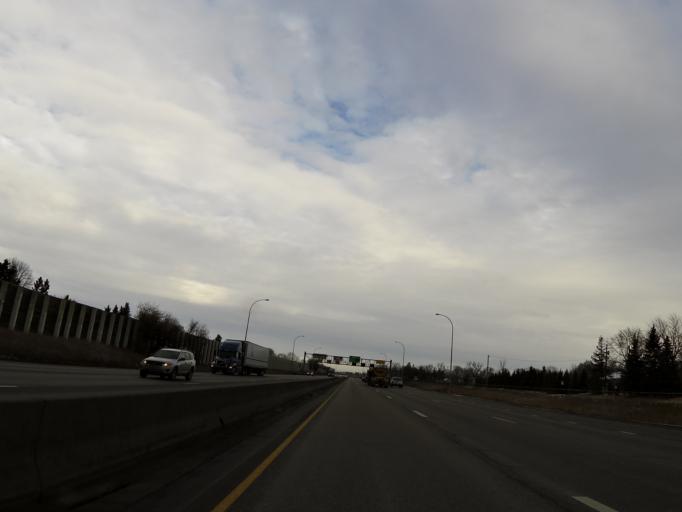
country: US
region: Minnesota
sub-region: Hennepin County
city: Bloomington
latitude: 44.8150
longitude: -93.2911
